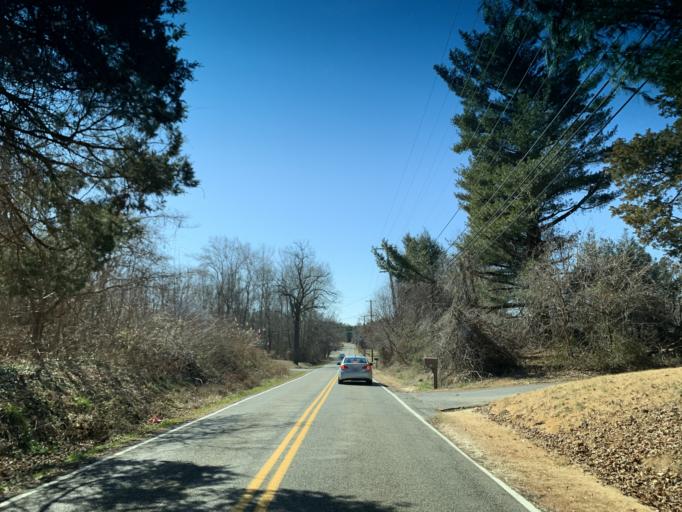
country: US
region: Maryland
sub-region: Cecil County
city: Elkton
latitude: 39.5182
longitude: -75.8230
